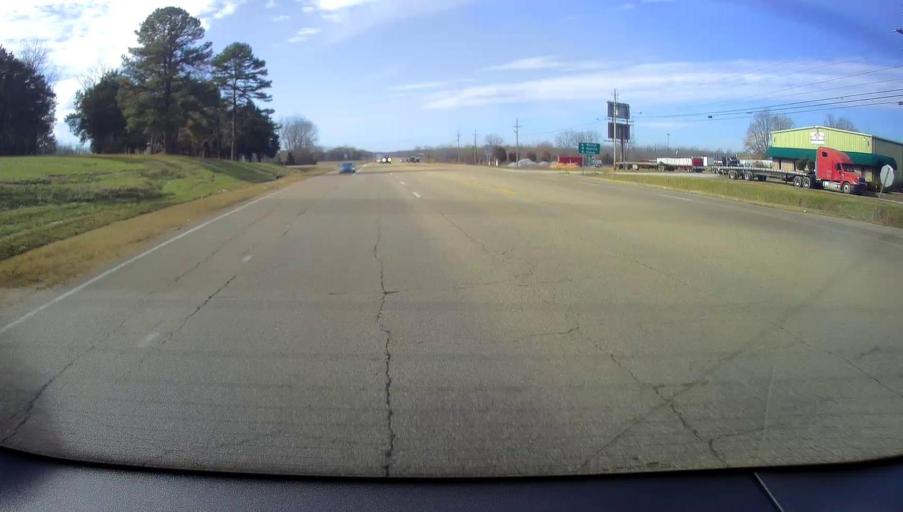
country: US
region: Mississippi
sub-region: Alcorn County
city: Corinth
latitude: 34.9309
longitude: -88.5686
